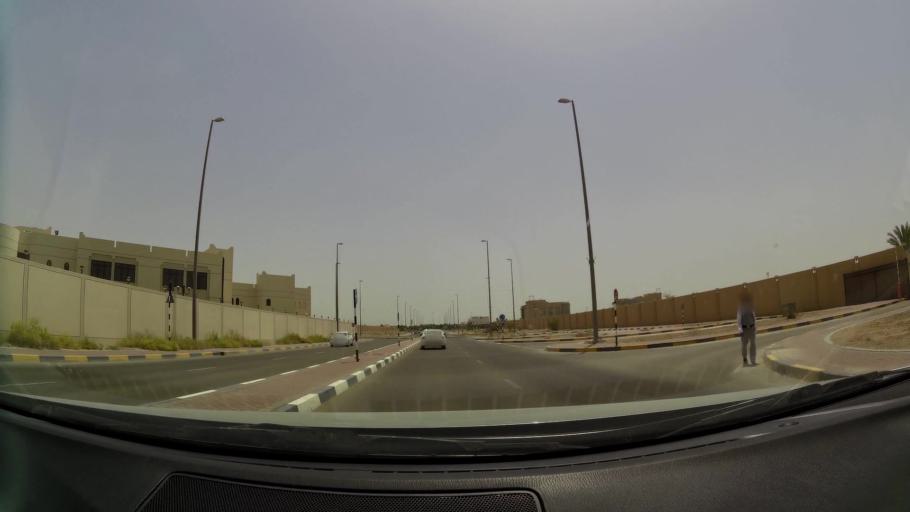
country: AE
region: Abu Dhabi
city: Al Ain
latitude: 24.1930
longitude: 55.7246
